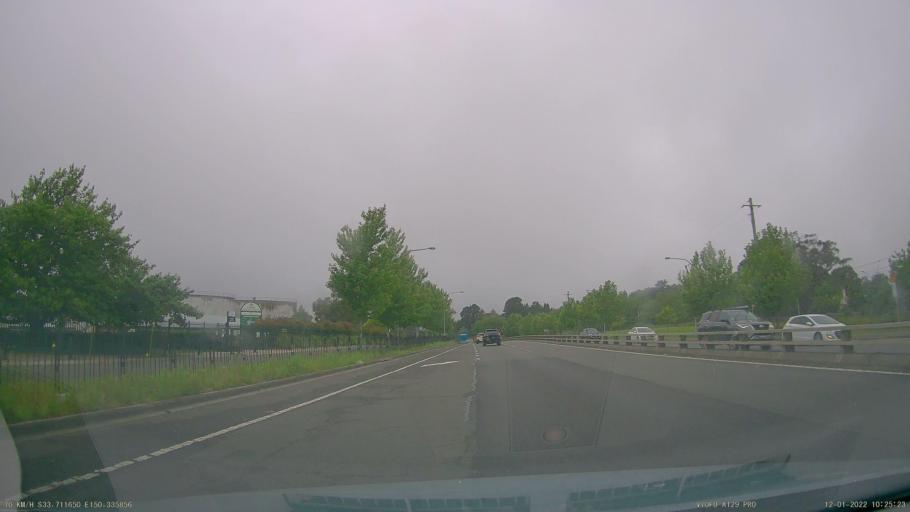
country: AU
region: New South Wales
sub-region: Blue Mountains Municipality
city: Leura
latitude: -33.7113
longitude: 150.3359
